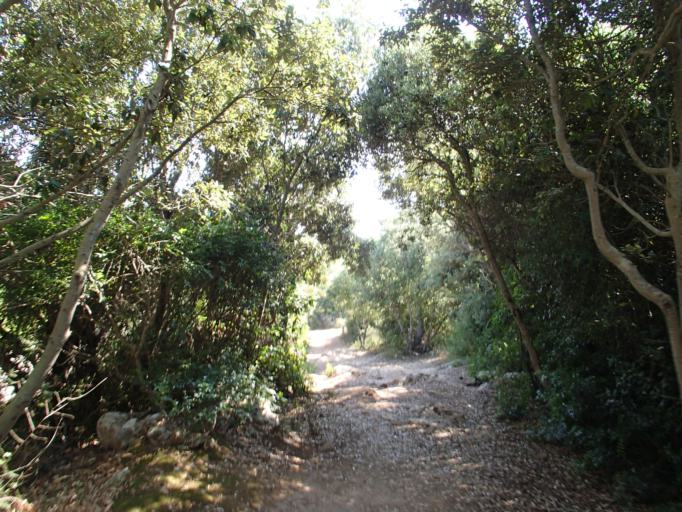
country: ES
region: Balearic Islands
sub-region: Illes Balears
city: Es Castell
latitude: 39.8424
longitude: 4.2943
